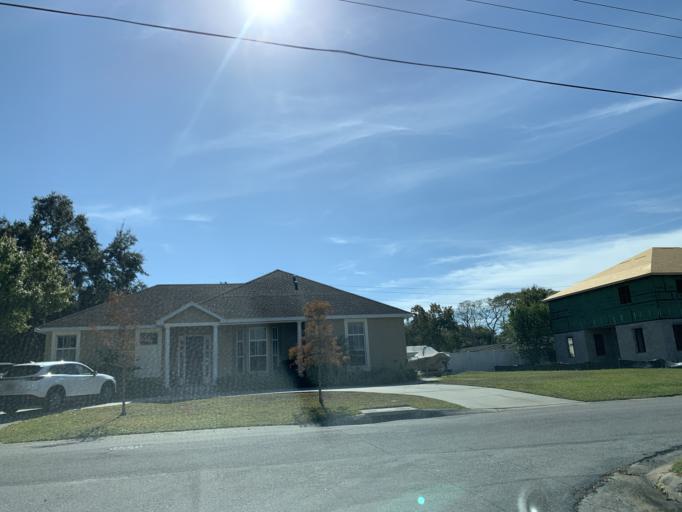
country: US
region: Florida
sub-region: Hillsborough County
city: Tampa
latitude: 27.8854
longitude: -82.5000
